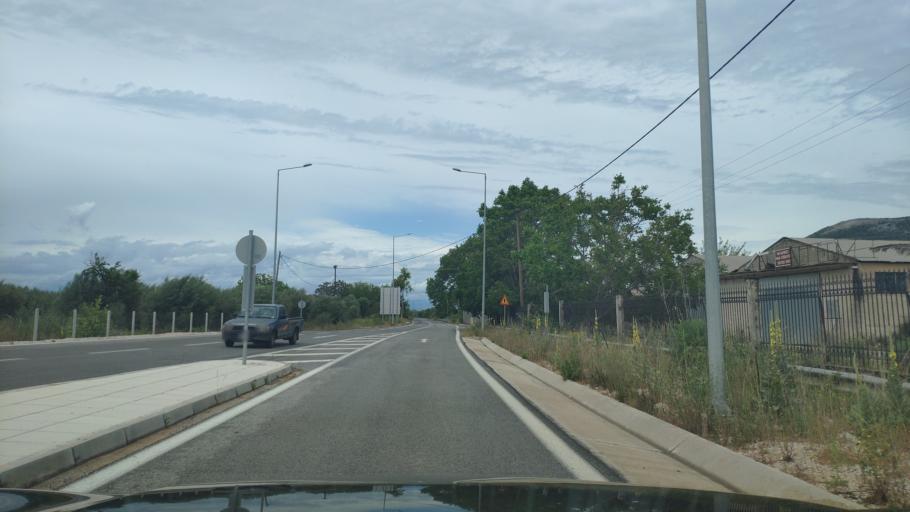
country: GR
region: West Greece
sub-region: Nomos Aitolias kai Akarnanias
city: Vonitsa
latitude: 38.8934
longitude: 20.8999
